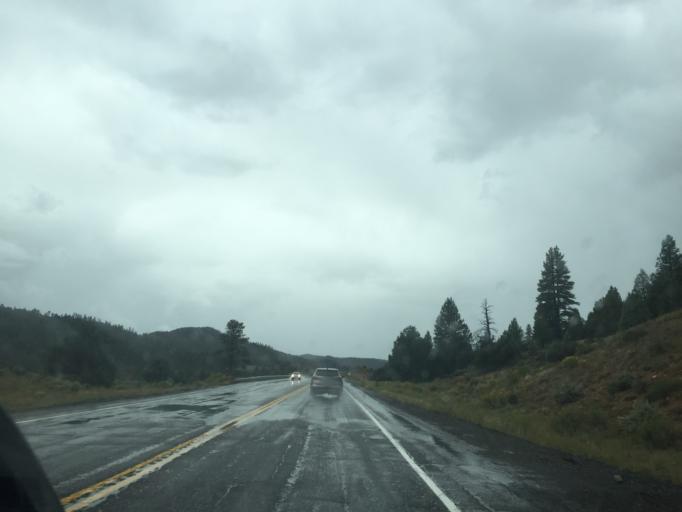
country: US
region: Utah
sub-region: Kane County
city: Kanab
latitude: 37.4013
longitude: -112.5566
